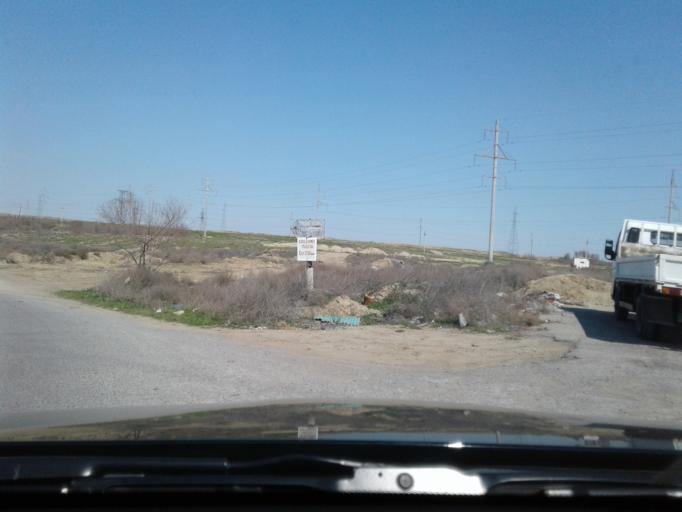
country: TM
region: Ahal
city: Abadan
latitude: 38.1101
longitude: 58.2038
